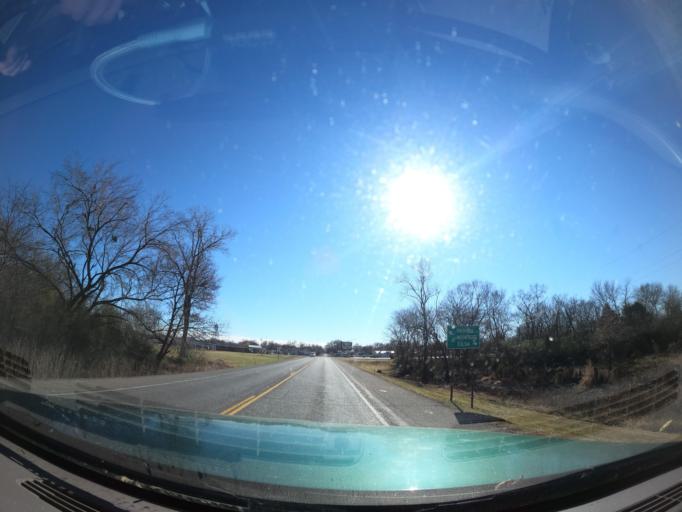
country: US
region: Oklahoma
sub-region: Muskogee County
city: Haskell
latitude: 35.8254
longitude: -95.6775
